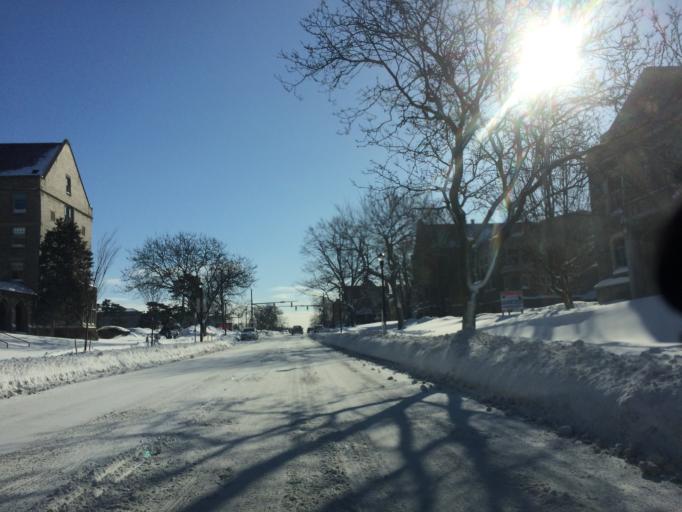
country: US
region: New York
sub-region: Monroe County
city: Rochester
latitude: 43.1581
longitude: -77.5922
